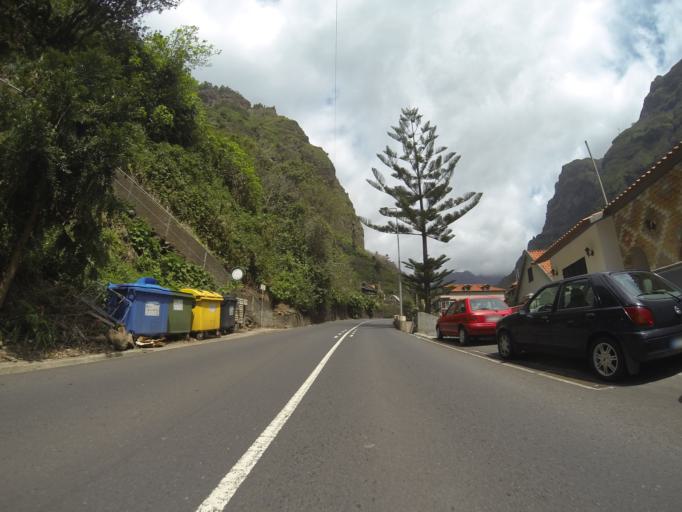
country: PT
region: Madeira
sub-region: Ribeira Brava
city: Campanario
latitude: 32.7119
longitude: -17.0352
